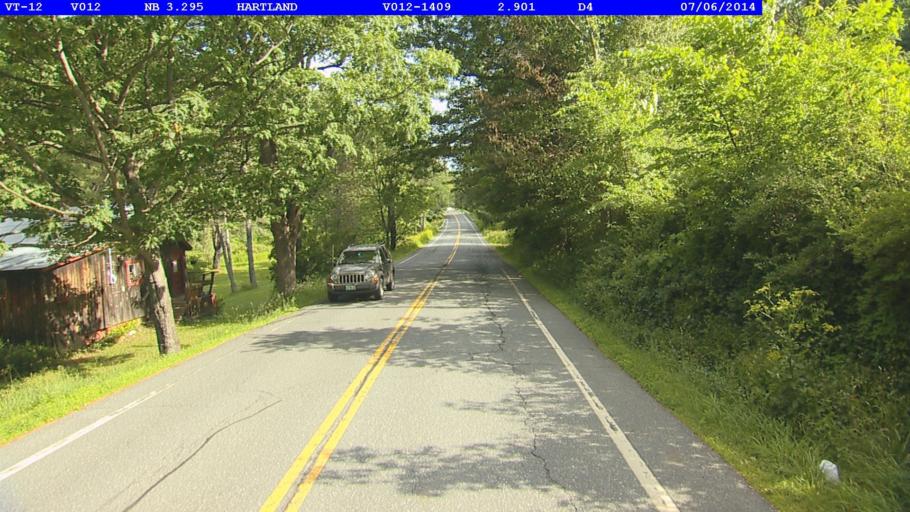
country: US
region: Vermont
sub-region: Windsor County
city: Woodstock
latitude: 43.5608
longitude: -72.4429
